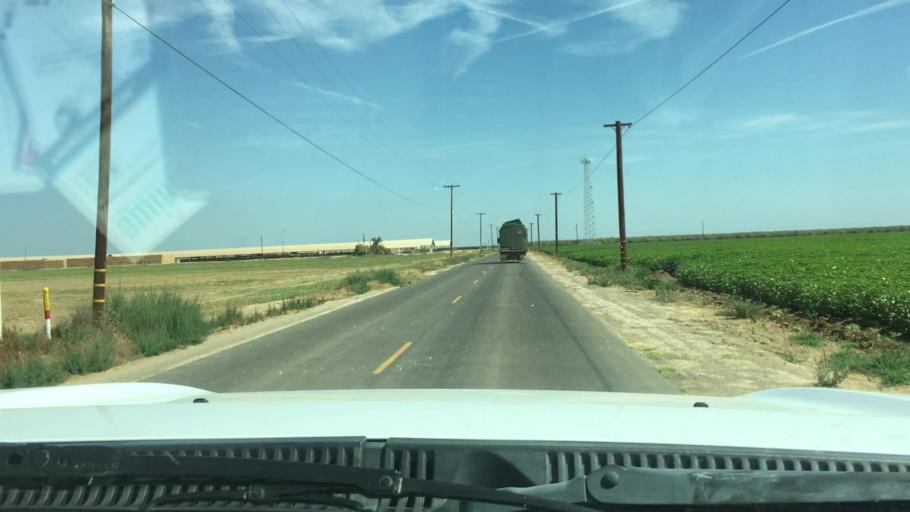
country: US
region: California
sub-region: Kern County
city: Shafter
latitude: 35.4672
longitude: -119.3681
